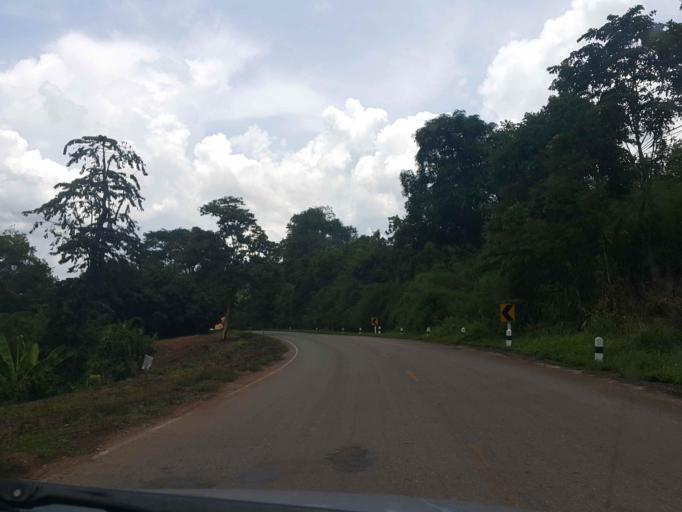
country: TH
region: Phayao
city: Chiang Muan
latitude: 18.9030
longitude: 100.1232
